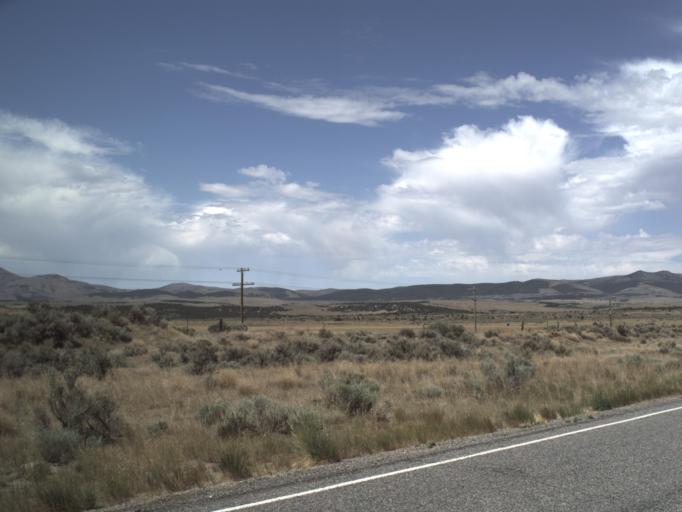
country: US
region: Utah
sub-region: Utah County
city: Genola
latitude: 39.9410
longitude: -112.1890
